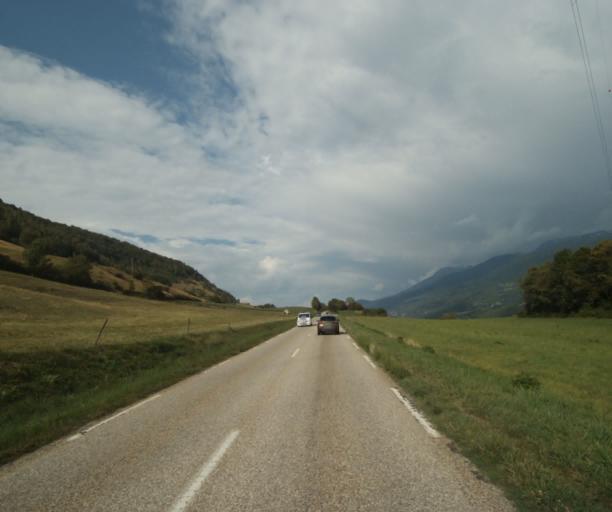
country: FR
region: Rhone-Alpes
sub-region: Departement de l'Isere
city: Vizille
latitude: 45.0940
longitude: 5.7815
